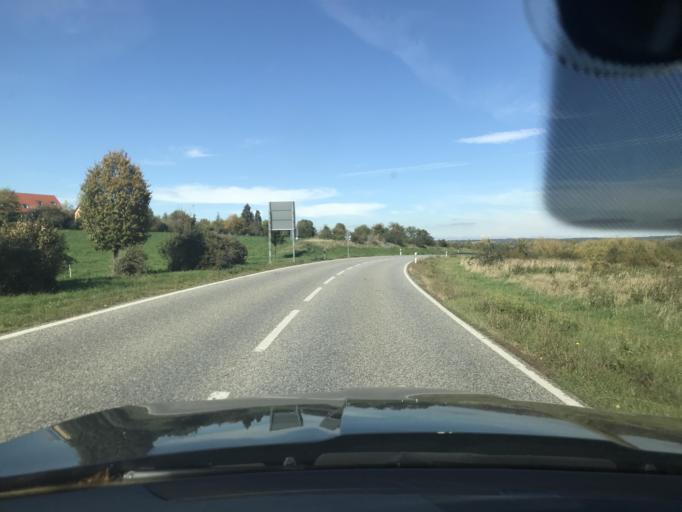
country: DE
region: Saxony-Anhalt
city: Neinstedt
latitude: 51.7520
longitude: 11.1008
